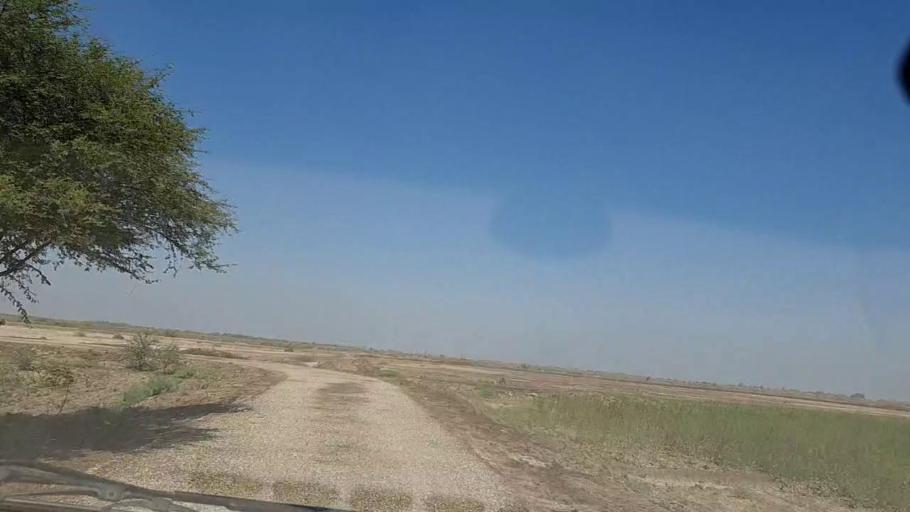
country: PK
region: Sindh
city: Mirpur Khas
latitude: 25.4384
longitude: 69.0512
